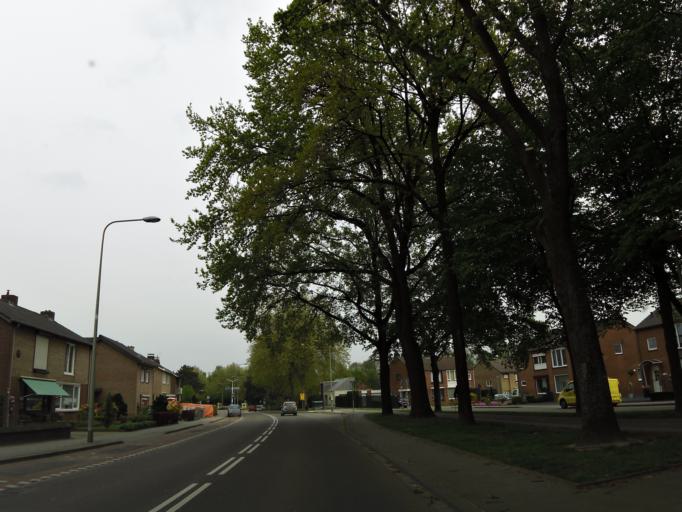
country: NL
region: Limburg
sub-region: Gemeente Brunssum
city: Brunssum
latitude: 50.9513
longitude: 5.9655
